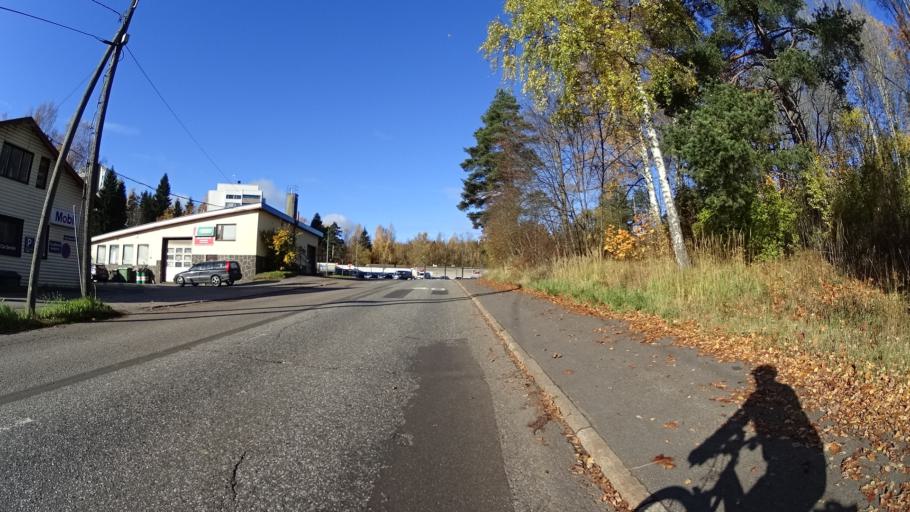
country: FI
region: Uusimaa
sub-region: Helsinki
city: Kilo
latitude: 60.3007
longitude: 24.8585
